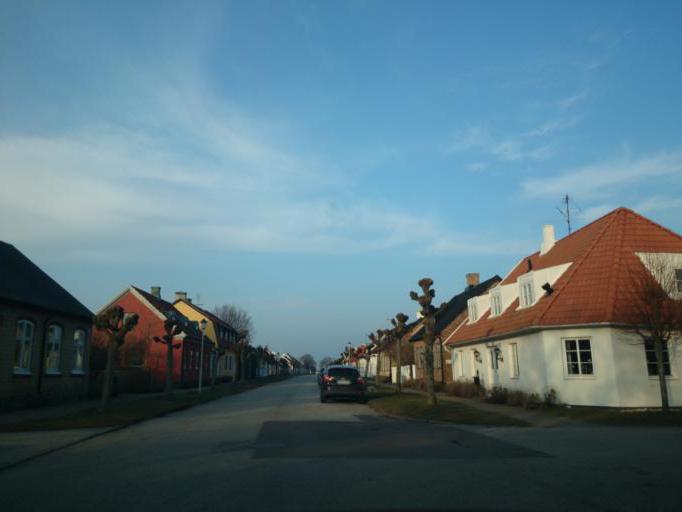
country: SE
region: Skane
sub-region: Vellinge Kommun
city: Skanor med Falsterbo
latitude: 55.4154
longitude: 12.8453
